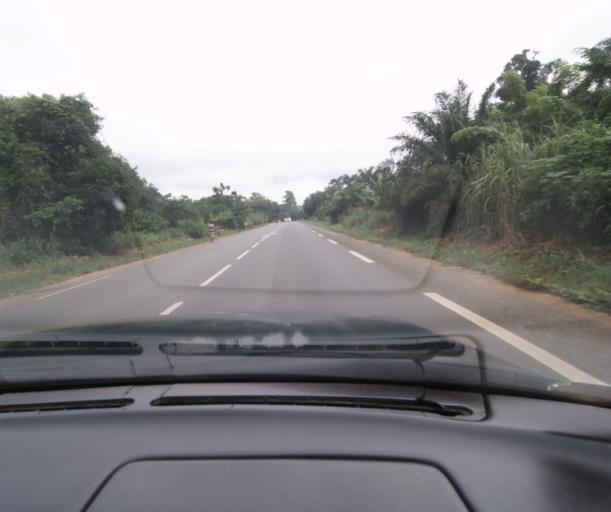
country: CM
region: Centre
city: Saa
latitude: 4.3354
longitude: 11.2846
